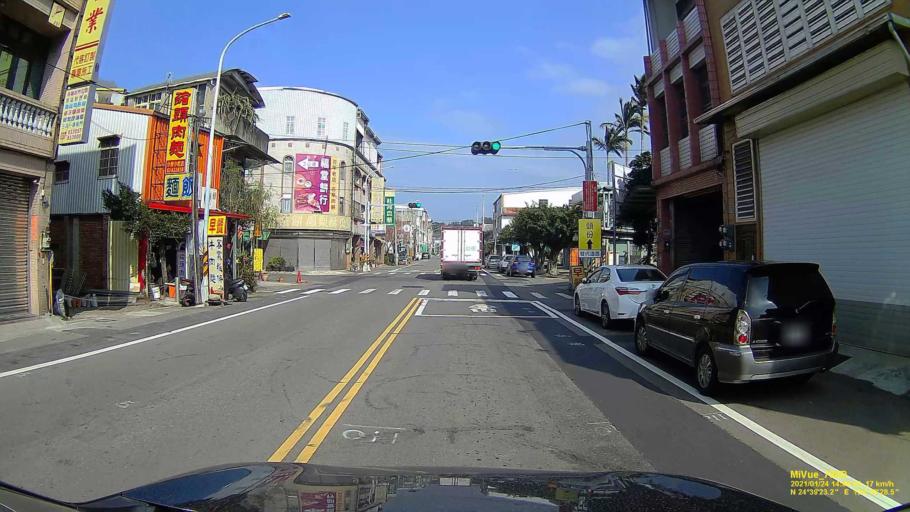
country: TW
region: Taiwan
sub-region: Hsinchu
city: Hsinchu
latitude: 24.6564
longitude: 120.9580
